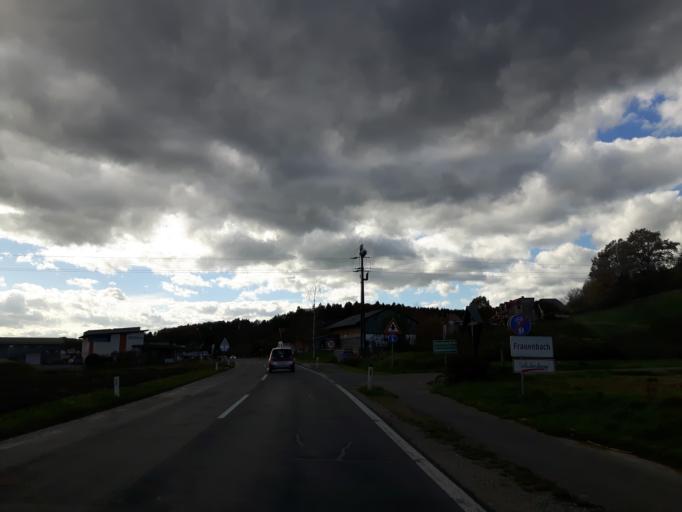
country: AT
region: Styria
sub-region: Politischer Bezirk Suedoststeiermark
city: Sankt Stefan im Rosental
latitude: 46.9166
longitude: 15.7135
